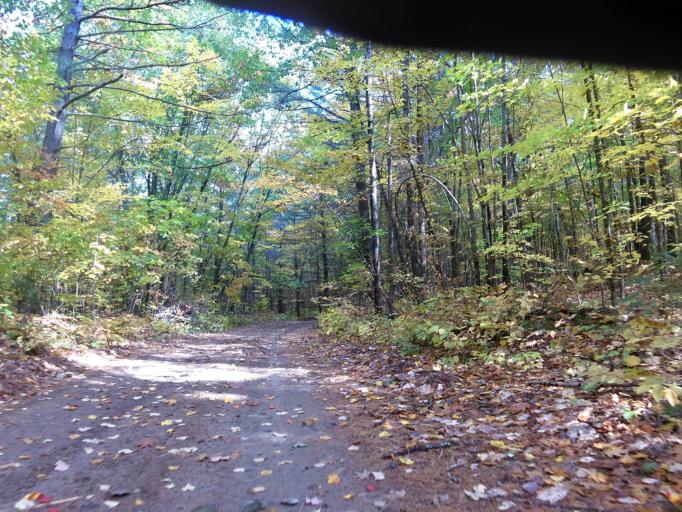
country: CA
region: Ontario
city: Petawawa
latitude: 45.8046
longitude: -77.2922
